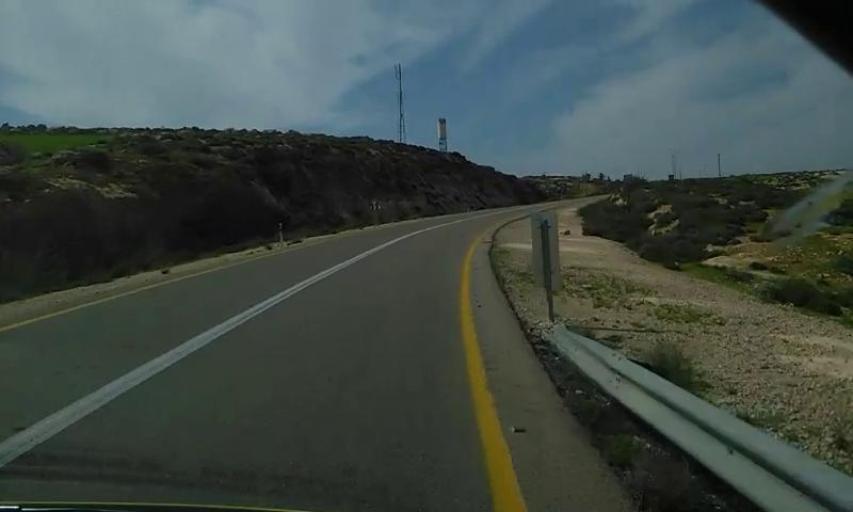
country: PS
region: West Bank
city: Az Zahiriyah
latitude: 31.3742
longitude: 35.0110
